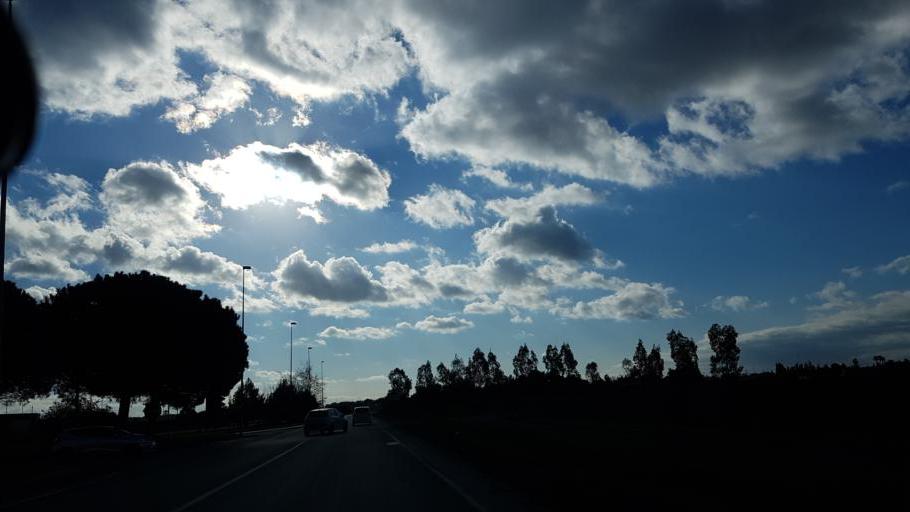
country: IT
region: Apulia
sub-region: Provincia di Brindisi
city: Brindisi
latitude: 40.6539
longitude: 17.9315
